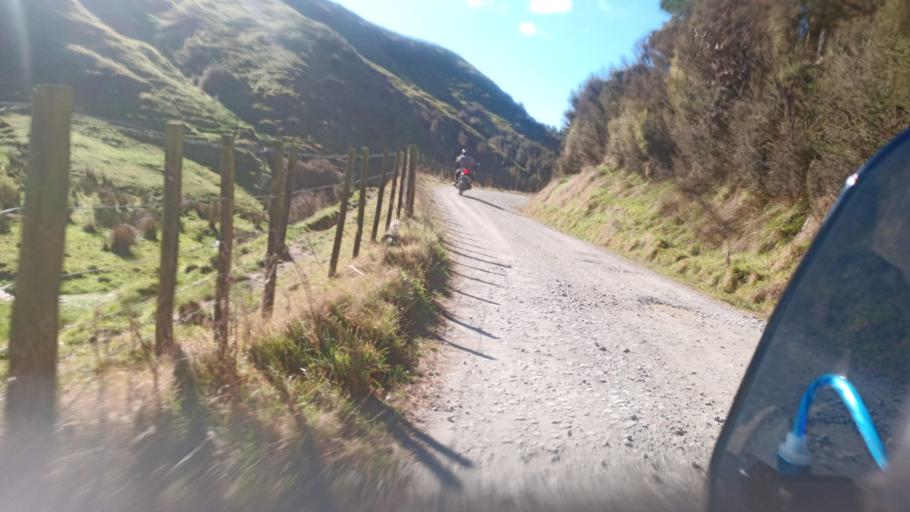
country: NZ
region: Hawke's Bay
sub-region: Wairoa District
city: Wairoa
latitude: -38.6591
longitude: 177.4894
